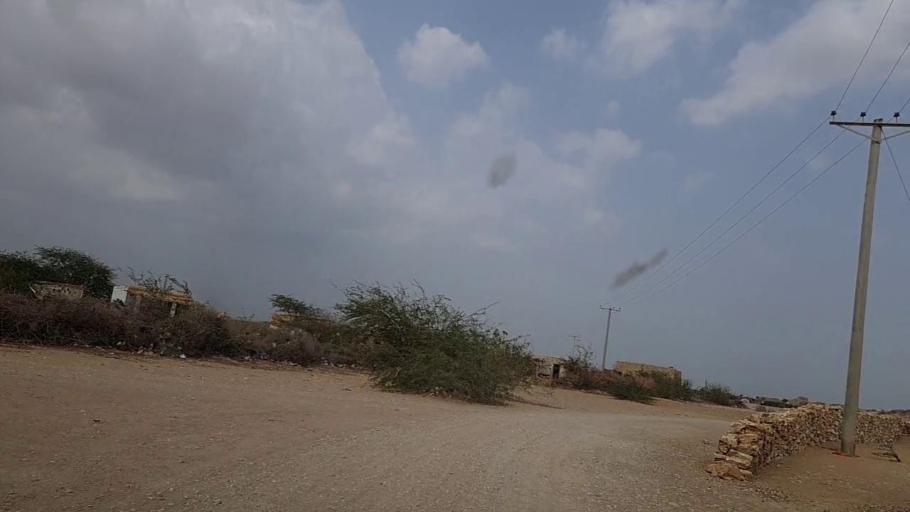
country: PK
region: Sindh
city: Kotri
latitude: 25.2868
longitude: 68.2175
